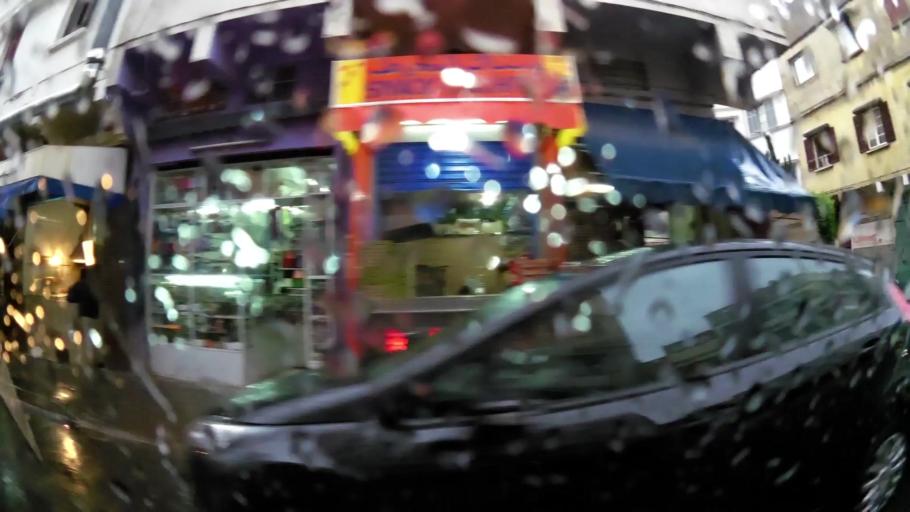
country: MA
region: Grand Casablanca
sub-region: Casablanca
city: Casablanca
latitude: 33.5633
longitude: -7.6072
